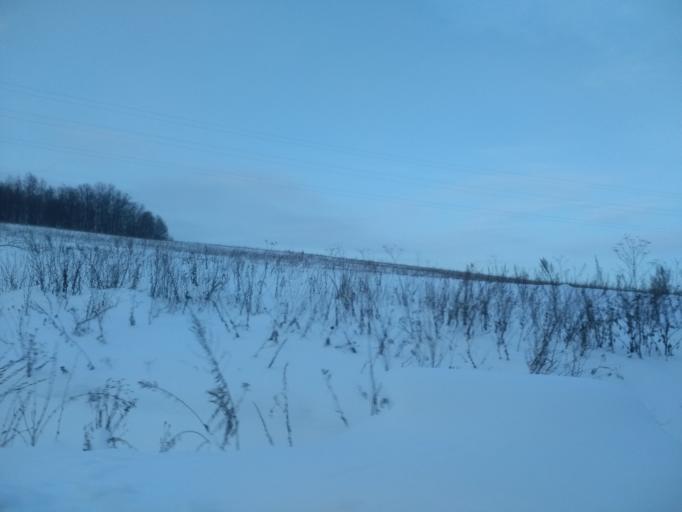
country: RU
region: Bashkortostan
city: Kudeyevskiy
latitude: 54.7159
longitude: 56.6143
